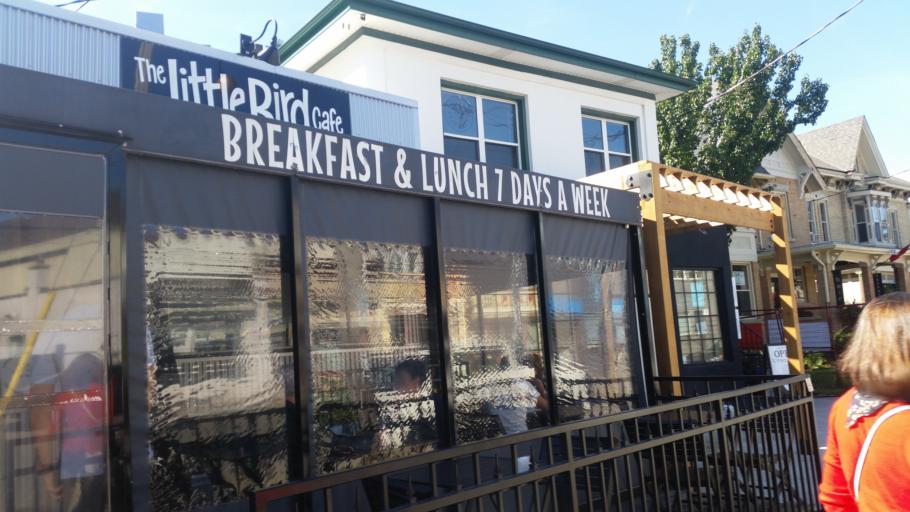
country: CA
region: Ontario
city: London
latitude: 42.9729
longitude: -81.2536
